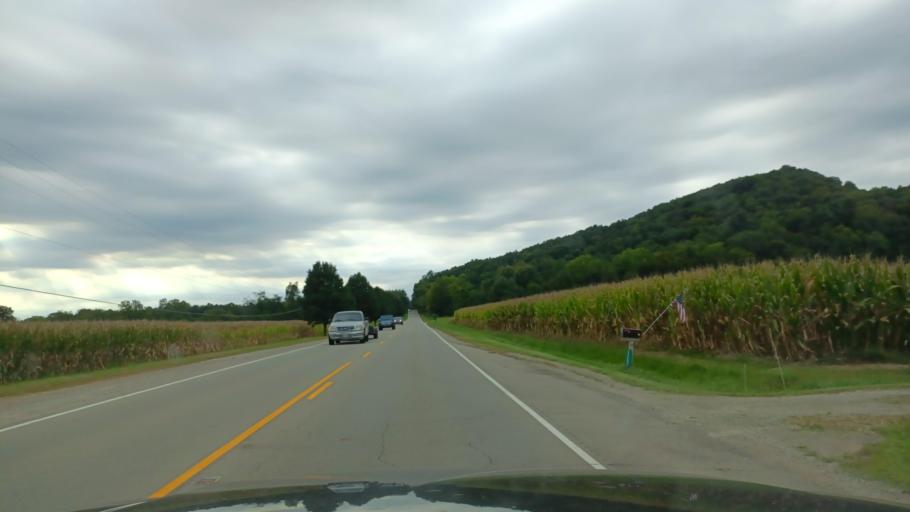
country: US
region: Ohio
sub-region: Ross County
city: Chillicothe
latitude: 39.2826
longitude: -82.8499
